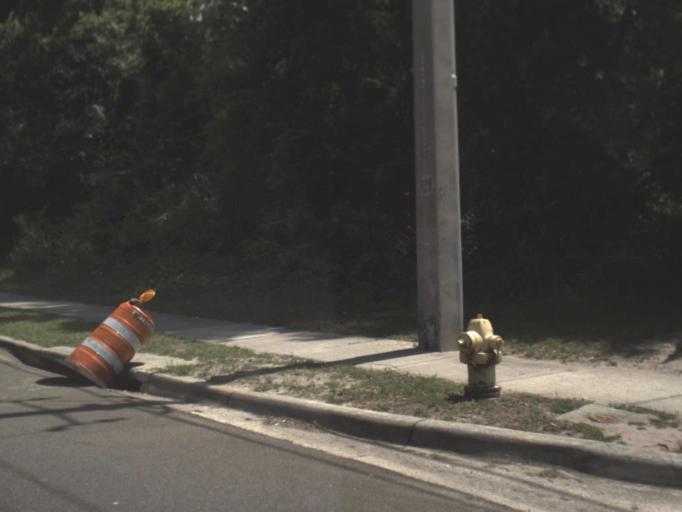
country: US
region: Florida
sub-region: Duval County
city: Jacksonville
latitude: 30.4266
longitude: -81.6947
